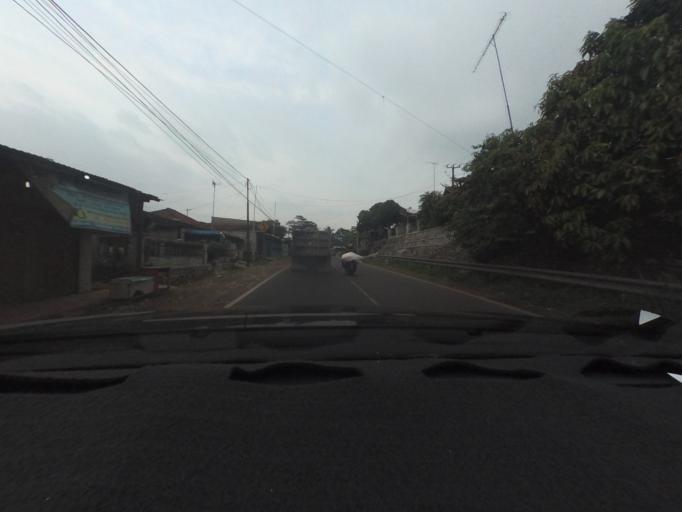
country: ID
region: West Java
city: Cicurug
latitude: -6.8107
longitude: 106.7693
